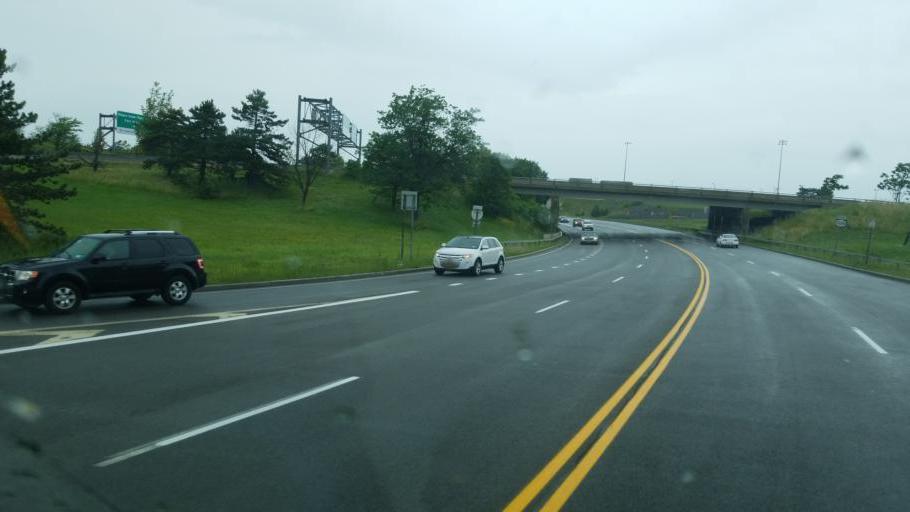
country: US
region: New York
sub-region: Niagara County
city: Lewiston
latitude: 43.1495
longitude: -79.0382
